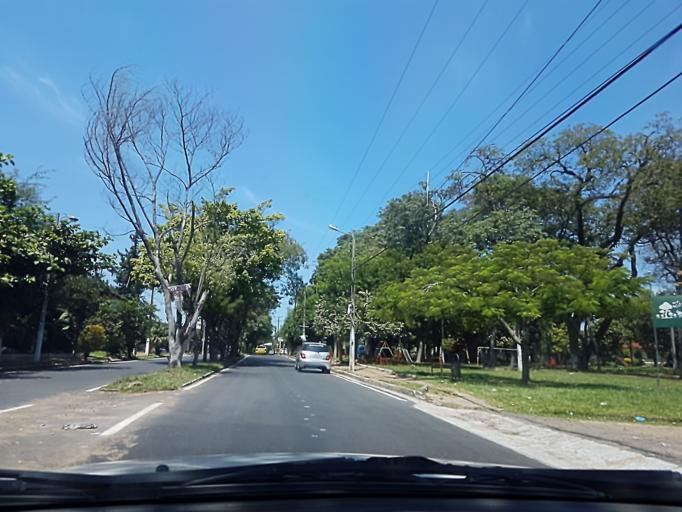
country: PY
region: Central
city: Fernando de la Mora
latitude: -25.2854
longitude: -57.5240
